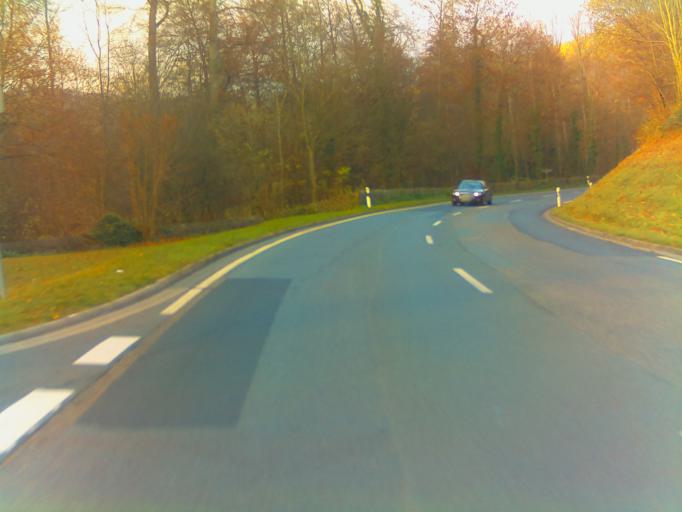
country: DE
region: Bavaria
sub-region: Regierungsbezirk Unterfranken
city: Weilbach
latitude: 49.6387
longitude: 9.2182
